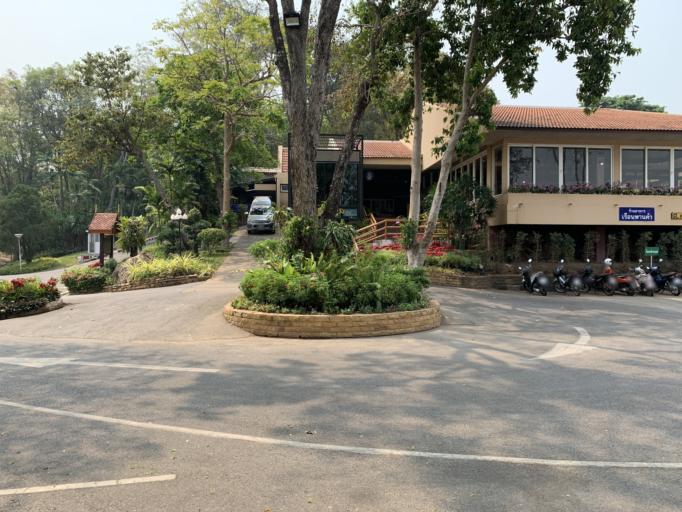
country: TH
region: Khon Kaen
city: Khuean Ubonrat
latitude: 16.7711
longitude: 102.6195
